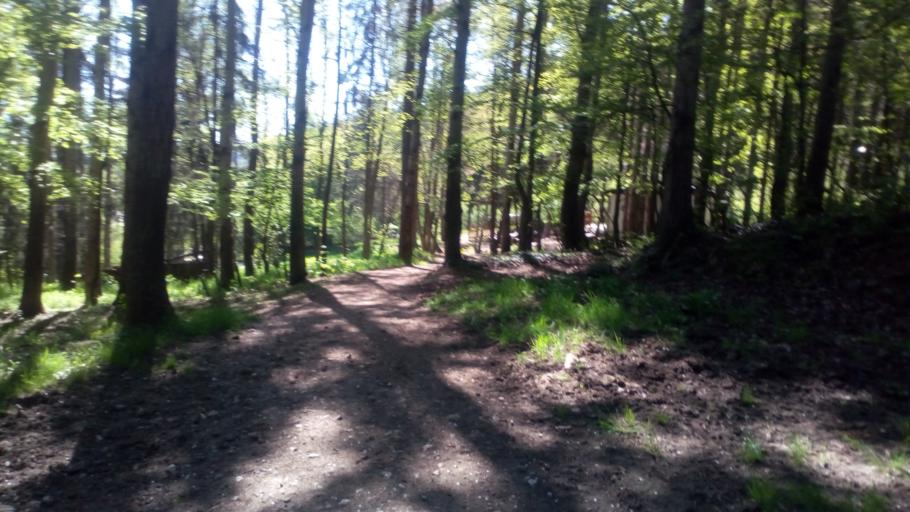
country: BG
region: Sofia-Capital
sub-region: Stolichna Obshtina
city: Sofia
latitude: 42.6210
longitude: 23.3057
